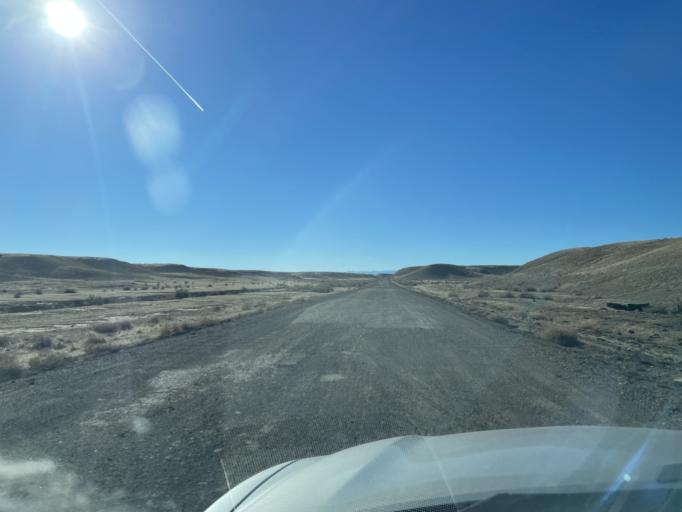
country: US
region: Colorado
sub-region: Mesa County
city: Loma
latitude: 39.2060
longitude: -109.0835
